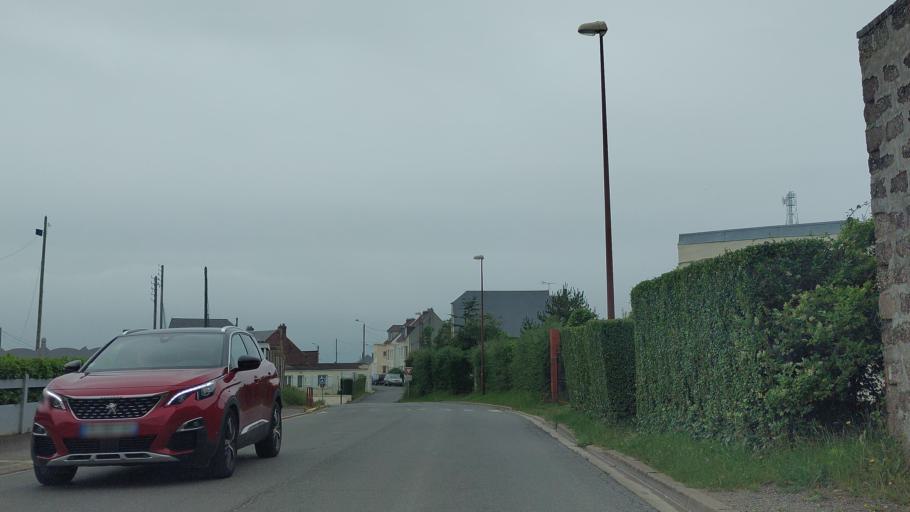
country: FR
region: Picardie
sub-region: Departement de la Somme
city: Ault
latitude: 50.1019
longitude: 1.4556
